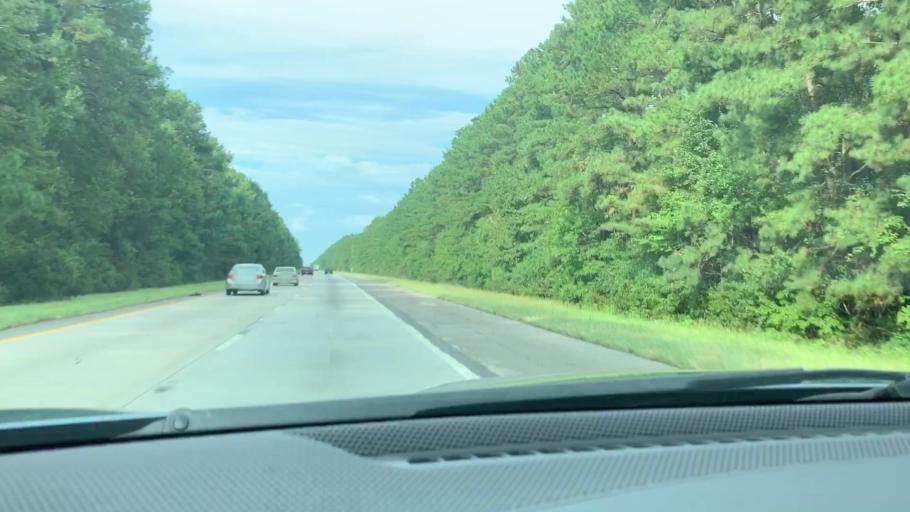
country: US
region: South Carolina
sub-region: Colleton County
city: Walterboro
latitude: 32.9649
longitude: -80.6772
